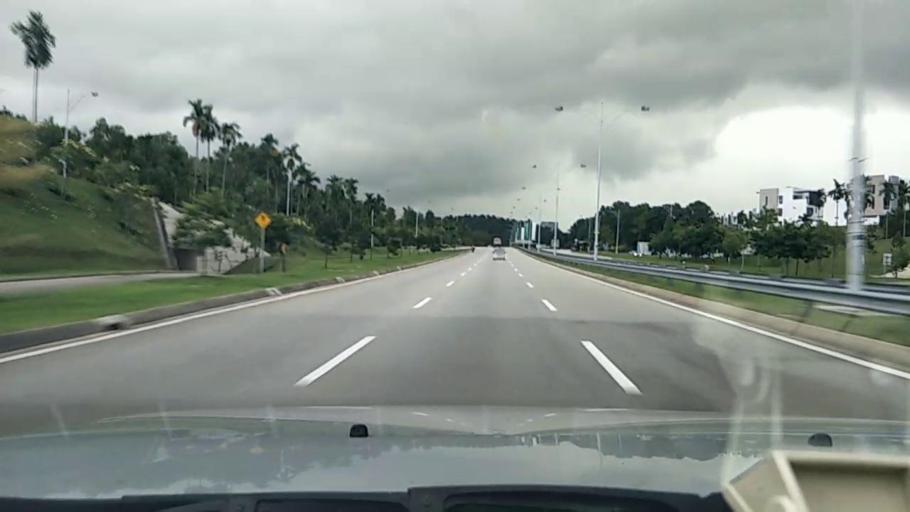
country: MY
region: Putrajaya
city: Putrajaya
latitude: 2.9430
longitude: 101.7140
